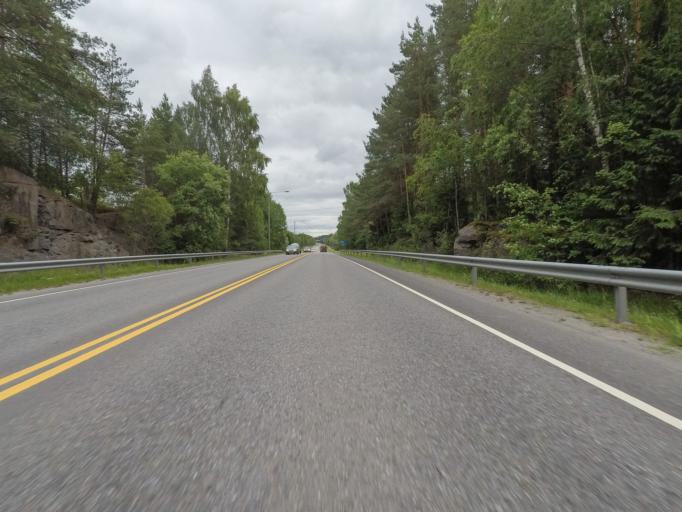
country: FI
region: Varsinais-Suomi
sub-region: Turku
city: Lieto
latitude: 60.4534
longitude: 22.4518
